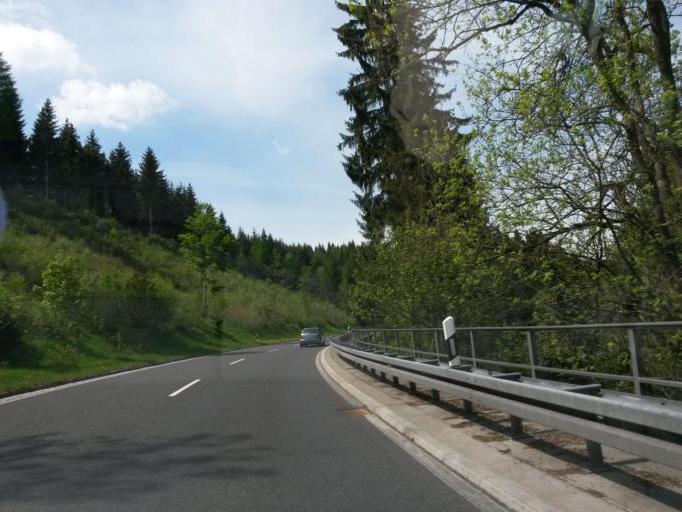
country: DE
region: Saxony
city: Zwota
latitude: 50.3569
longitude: 12.4216
